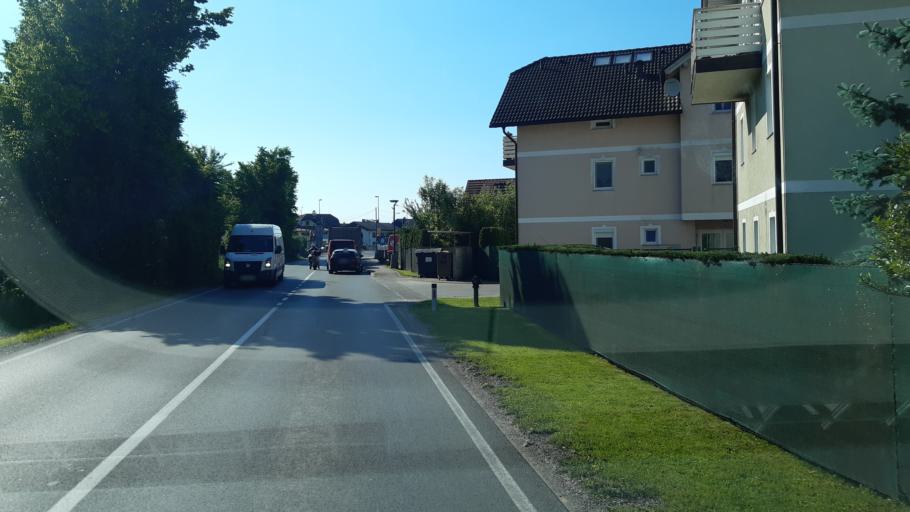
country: SI
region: Komenda
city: Moste
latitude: 46.1961
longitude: 14.5425
